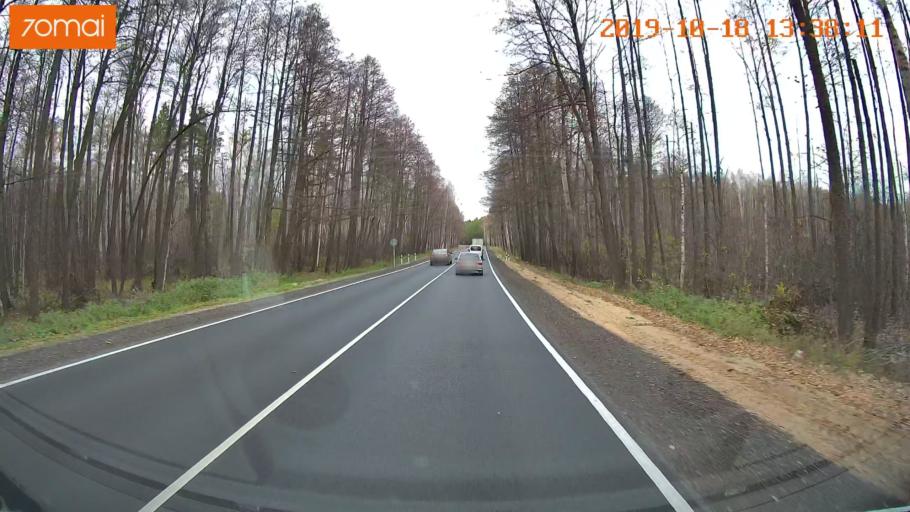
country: RU
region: Rjazan
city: Solotcha
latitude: 54.8872
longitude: 40.0014
